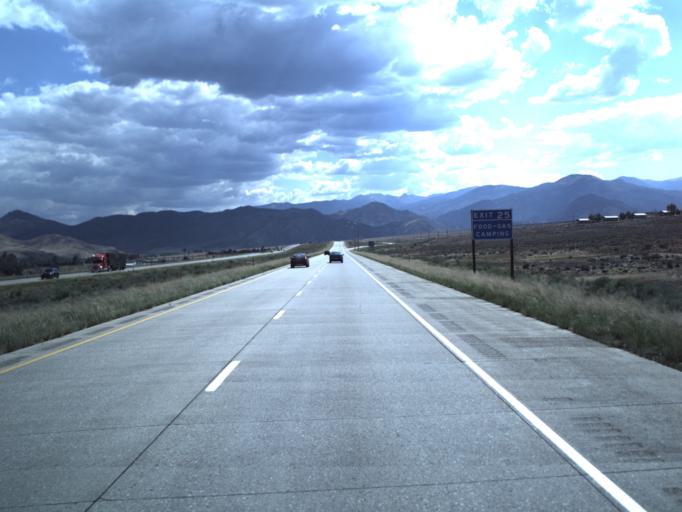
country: US
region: Utah
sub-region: Sevier County
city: Monroe
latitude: 38.6361
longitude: -112.2222
